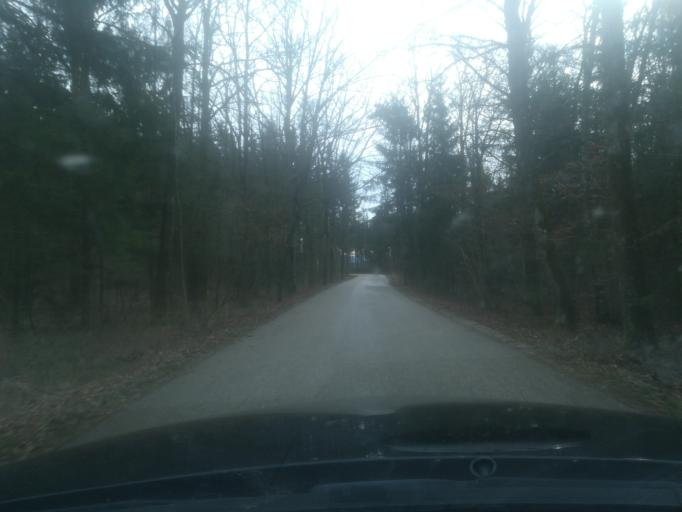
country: AT
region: Upper Austria
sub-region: Wels-Land
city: Gunskirchen
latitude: 48.1123
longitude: 13.9391
